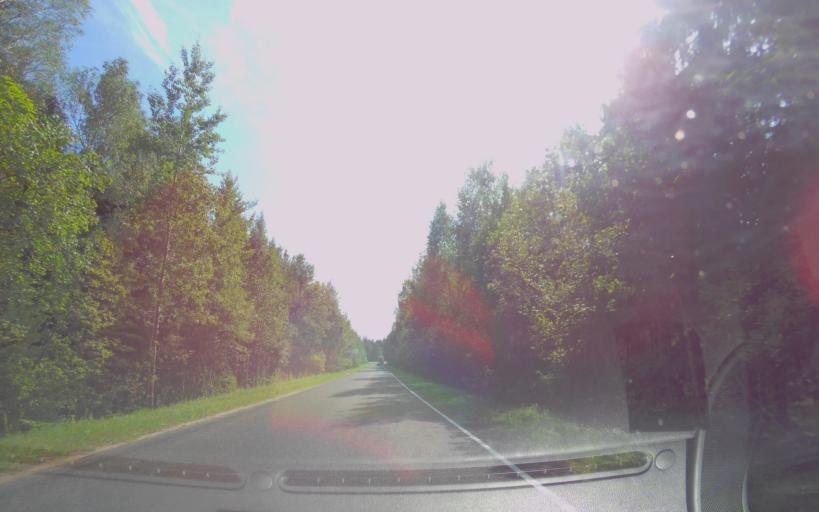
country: BY
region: Minsk
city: Horad Barysaw
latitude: 54.1760
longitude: 28.5720
